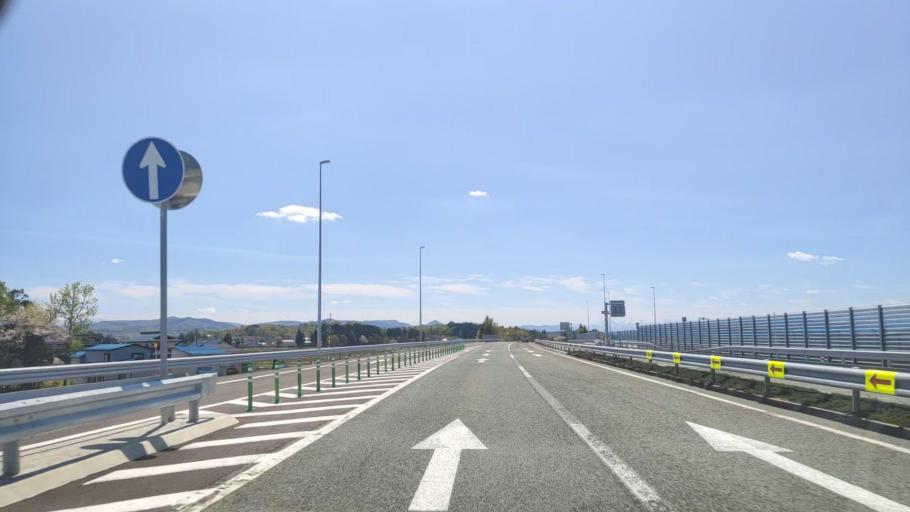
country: JP
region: Akita
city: Yokotemachi
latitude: 39.3254
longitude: 140.5130
